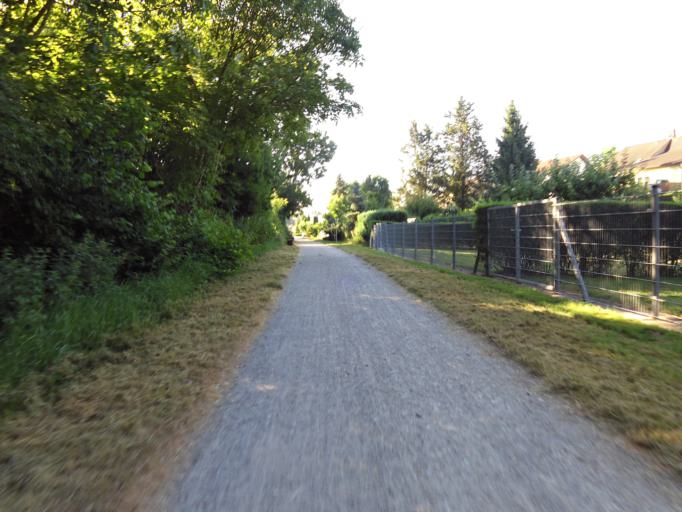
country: DE
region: Rheinland-Pfalz
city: Mutterstadt
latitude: 49.4616
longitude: 8.3688
